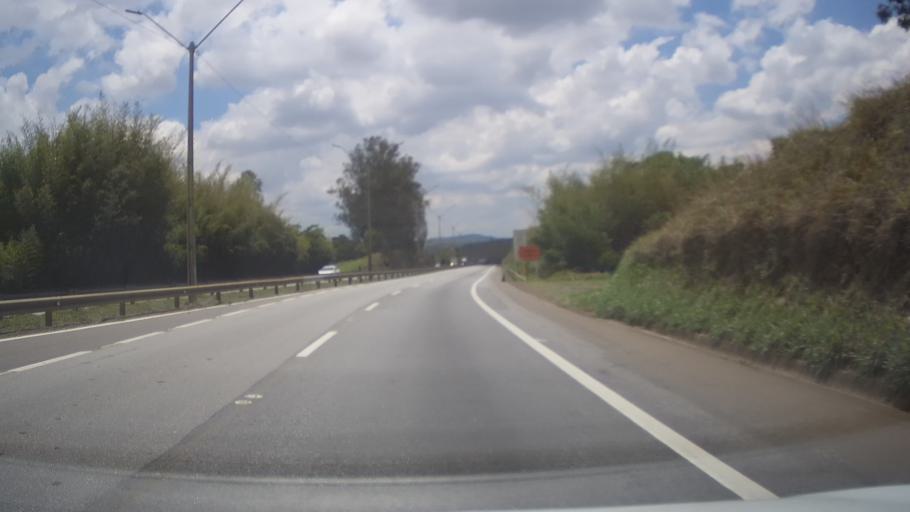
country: BR
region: Minas Gerais
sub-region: Tres Coracoes
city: Tres Coracoes
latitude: -21.6884
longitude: -45.3477
